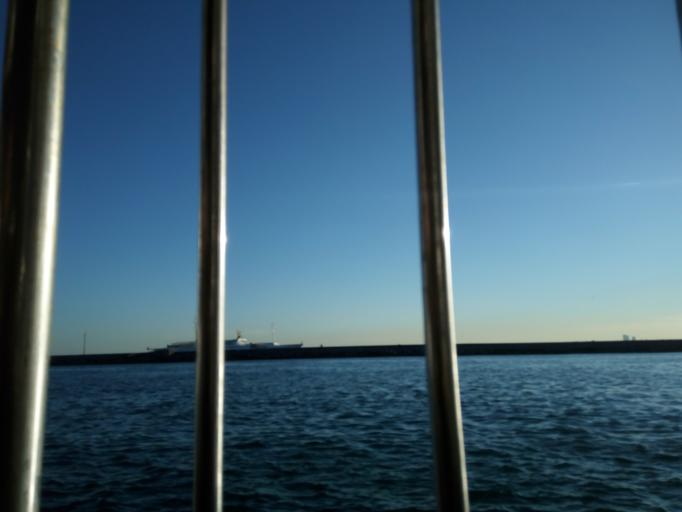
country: TR
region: Istanbul
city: UEskuedar
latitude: 41.0031
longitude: 29.0083
